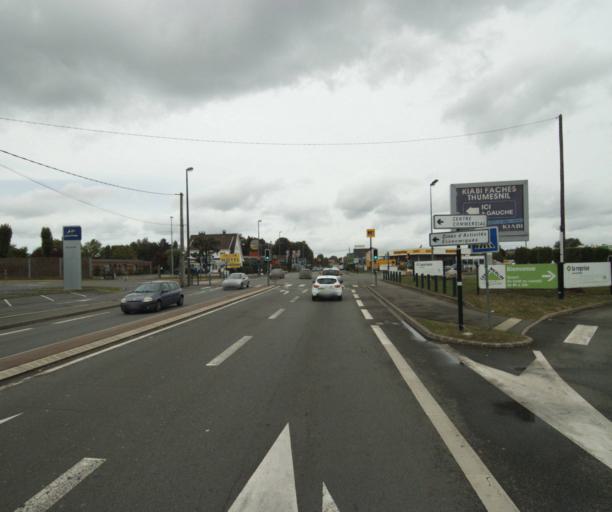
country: FR
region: Nord-Pas-de-Calais
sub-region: Departement du Nord
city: Vendeville
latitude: 50.5850
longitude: 3.0880
